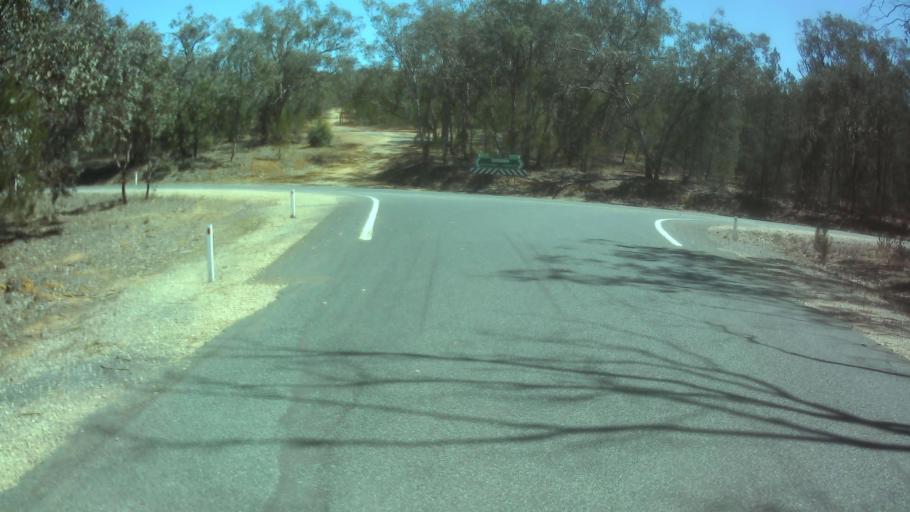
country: AU
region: New South Wales
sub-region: Weddin
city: Grenfell
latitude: -33.9391
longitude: 148.3849
